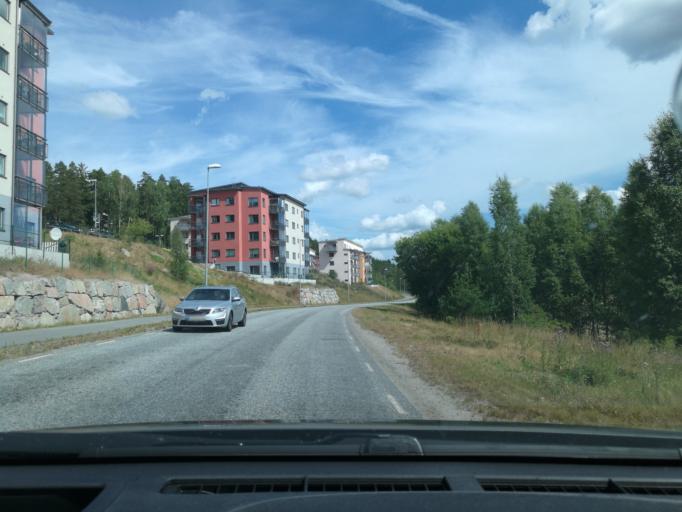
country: SE
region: Stockholm
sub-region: Sigtuna Kommun
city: Marsta
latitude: 59.6109
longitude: 17.8317
